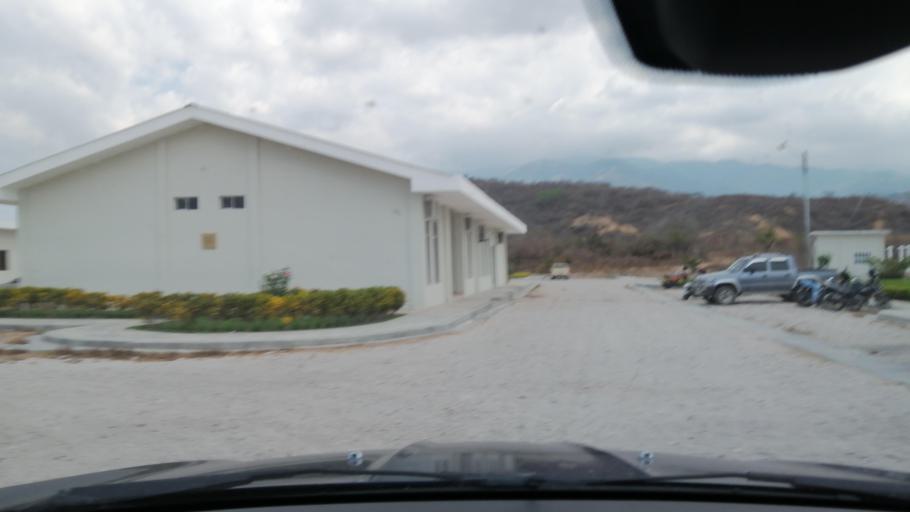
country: SV
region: Santa Ana
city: Metapan
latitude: 14.3392
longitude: -89.4476
